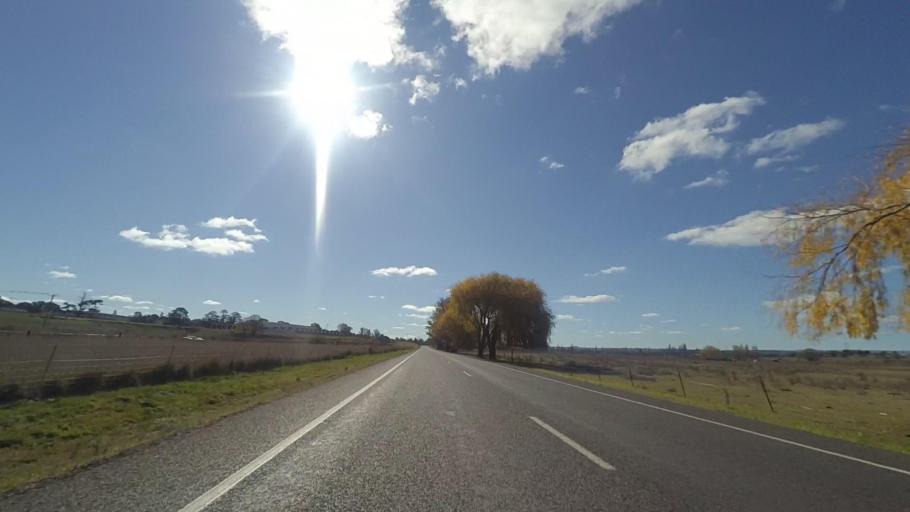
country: AU
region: New South Wales
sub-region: Bathurst Regional
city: Bathurst
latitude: -33.4472
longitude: 149.5789
